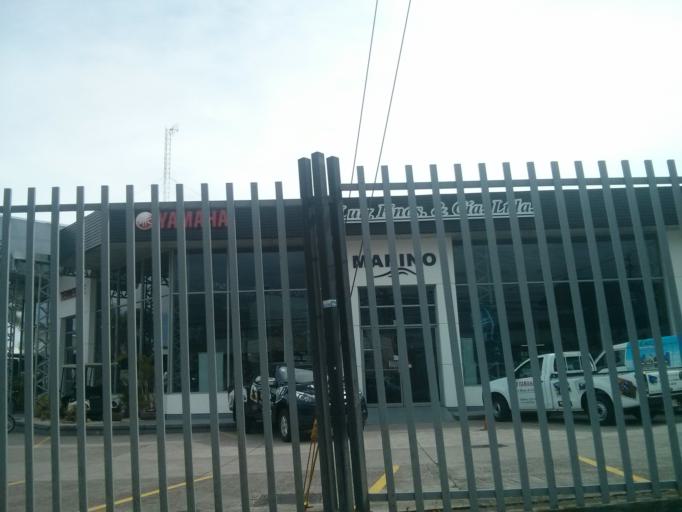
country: CR
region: San Jose
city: Colima
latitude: 9.9484
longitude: -84.0954
